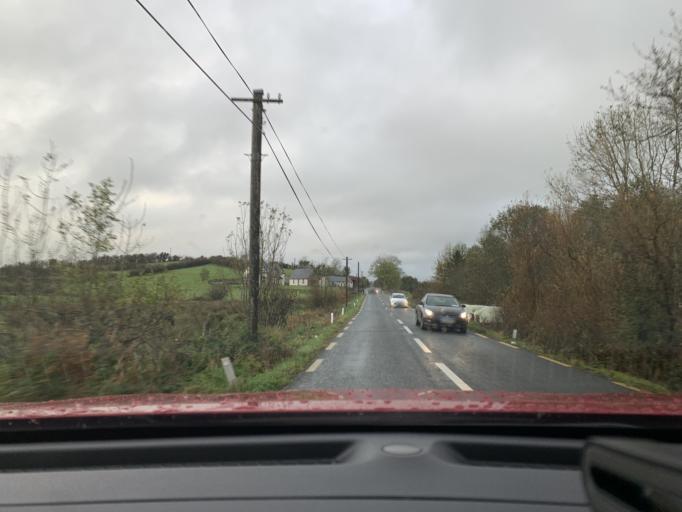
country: IE
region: Connaught
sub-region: Sligo
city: Ballymote
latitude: 54.0415
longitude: -8.5229
